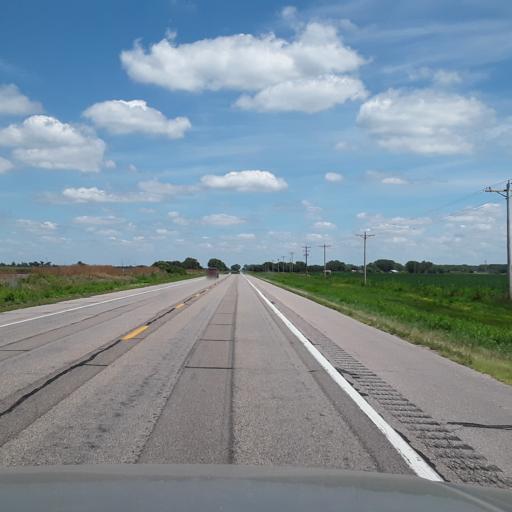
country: US
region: Nebraska
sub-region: Nance County
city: Genoa
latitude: 41.3373
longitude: -97.6131
